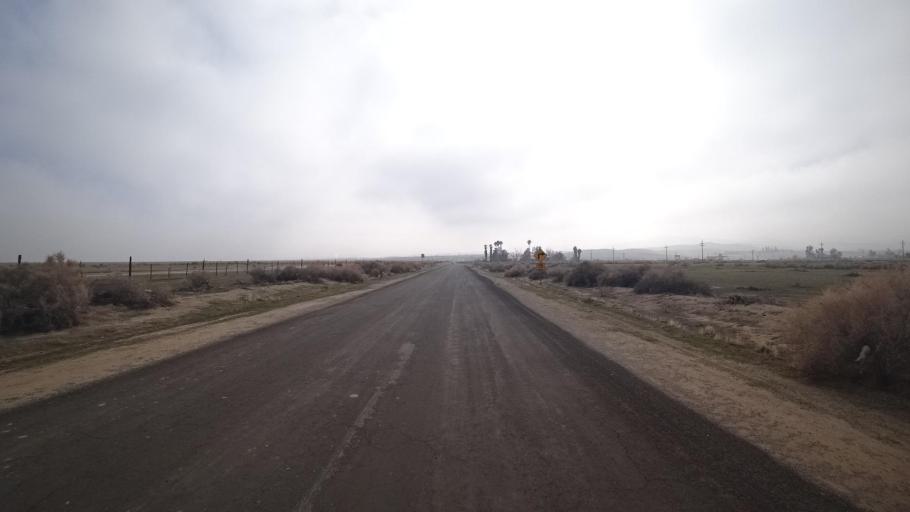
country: US
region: California
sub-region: Kern County
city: Maricopa
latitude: 35.0486
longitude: -119.3492
